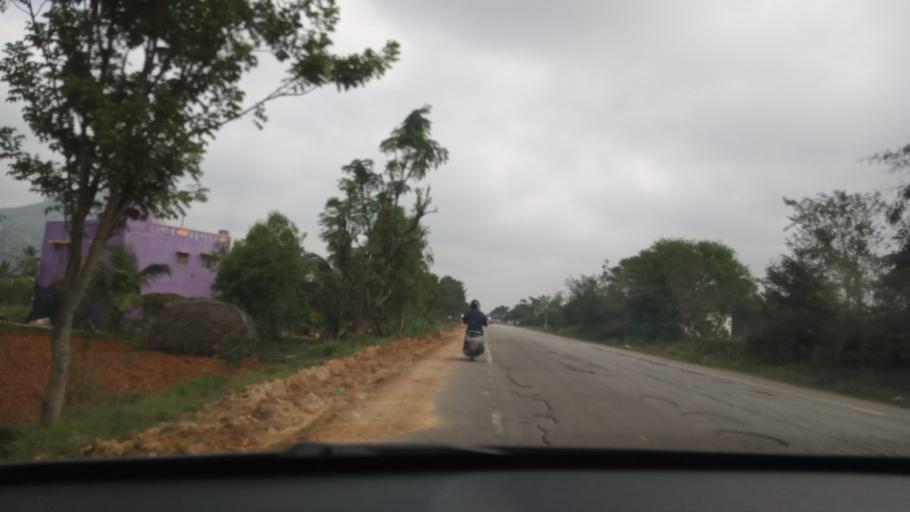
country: IN
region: Karnataka
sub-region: Chikkaballapur
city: Chintamani
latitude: 13.3310
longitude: 77.9975
